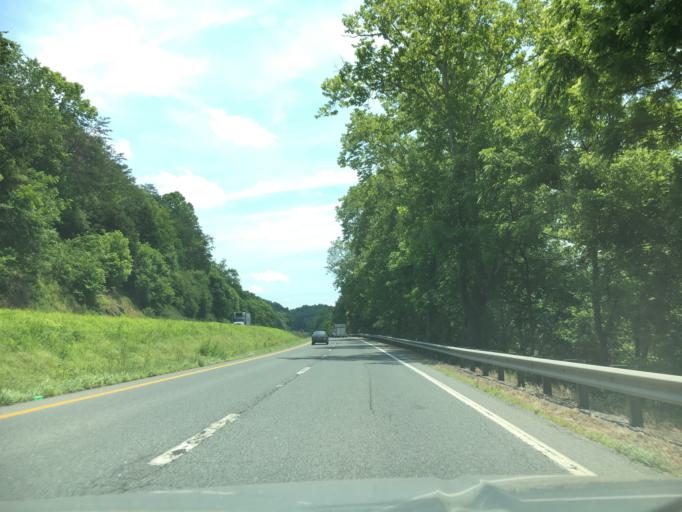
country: US
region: Virginia
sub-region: Campbell County
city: Concord
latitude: 37.3789
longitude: -79.0477
